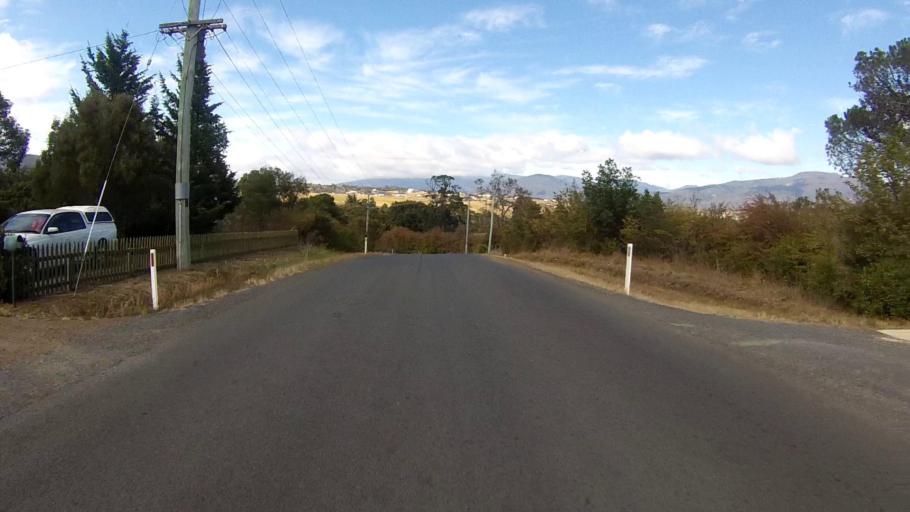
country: AU
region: Tasmania
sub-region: Brighton
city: Old Beach
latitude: -42.7519
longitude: 147.2792
